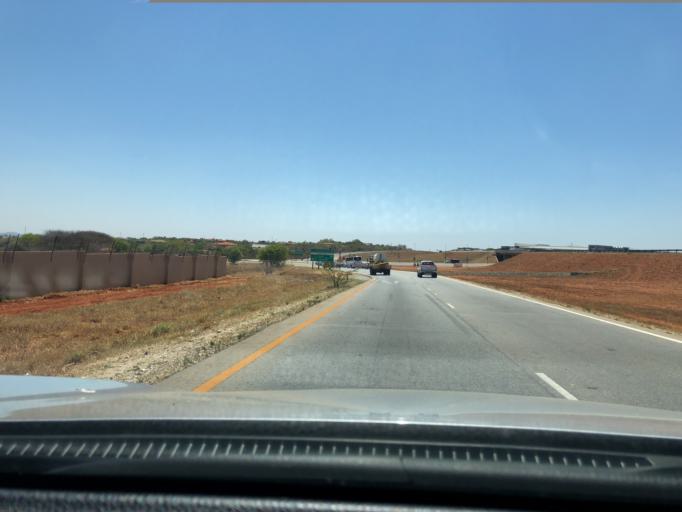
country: ZA
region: Limpopo
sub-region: Capricorn District Municipality
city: Polokwane
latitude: -23.8807
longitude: 29.5073
